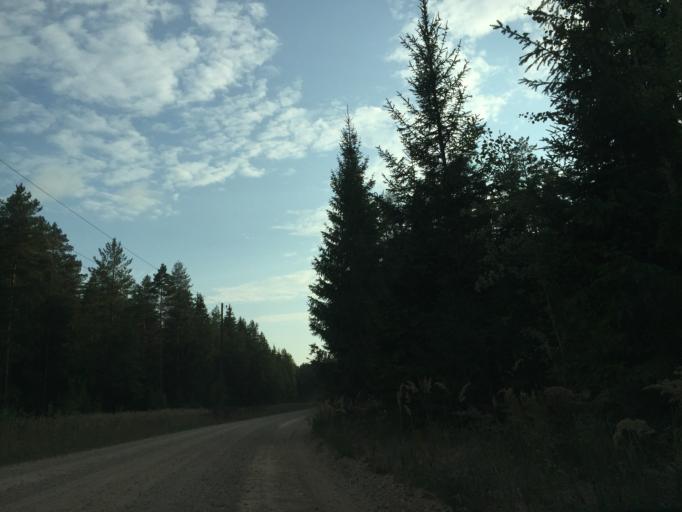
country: LV
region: Ikskile
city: Ikskile
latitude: 56.8025
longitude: 24.4400
